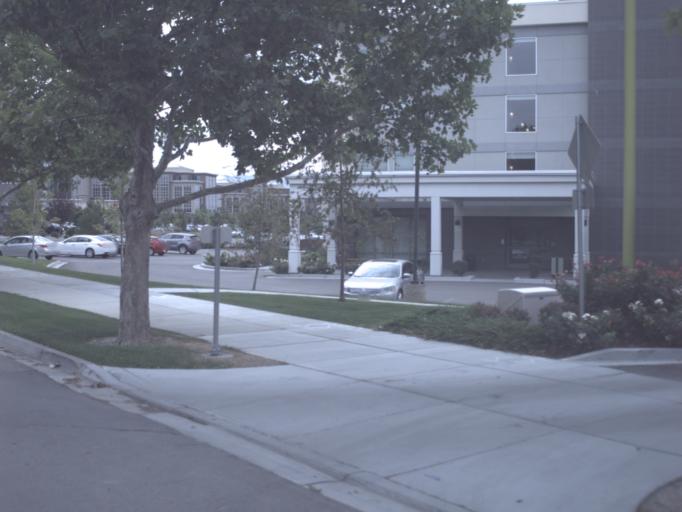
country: US
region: Utah
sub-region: Utah County
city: Lehi
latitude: 40.4311
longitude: -111.8986
